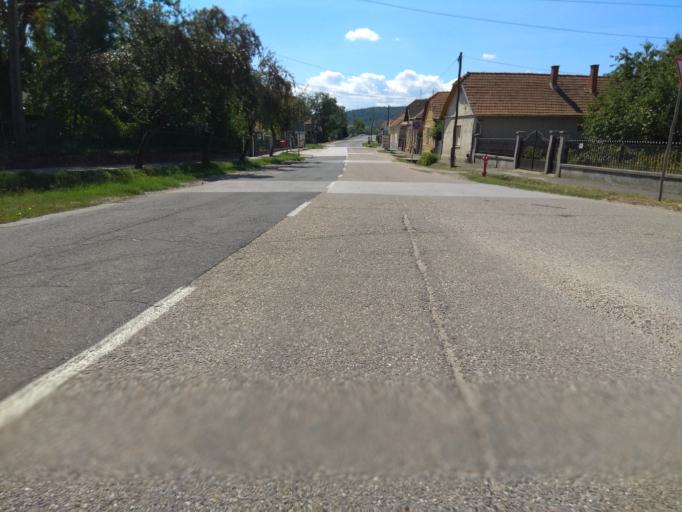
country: HU
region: Borsod-Abauj-Zemplen
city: Sajokaza
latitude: 48.2835
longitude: 20.5827
